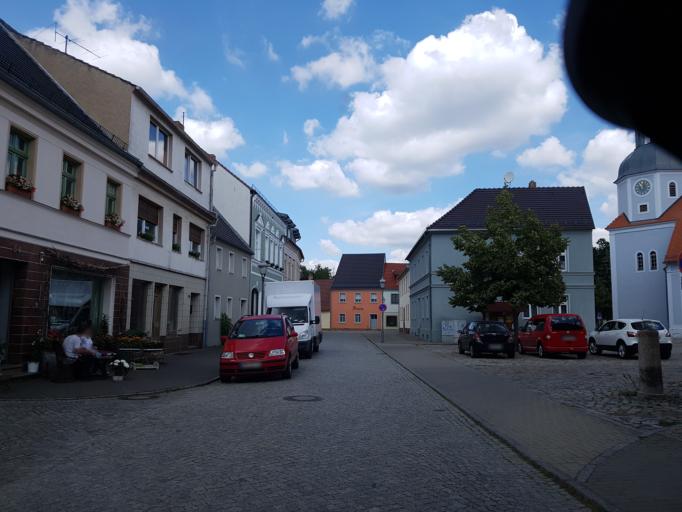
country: DE
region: Brandenburg
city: Drebkau
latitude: 51.6581
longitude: 14.2196
